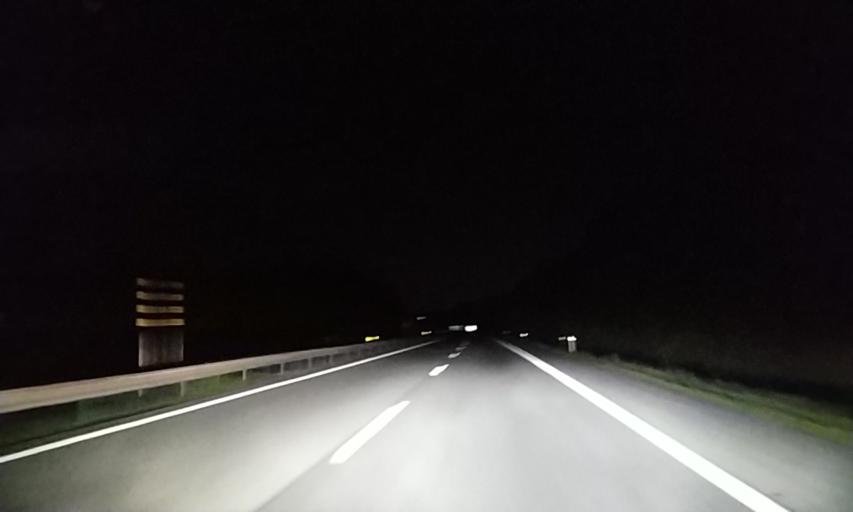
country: PT
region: Aveiro
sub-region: Estarreja
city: Salreu
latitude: 40.7340
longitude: -8.5233
